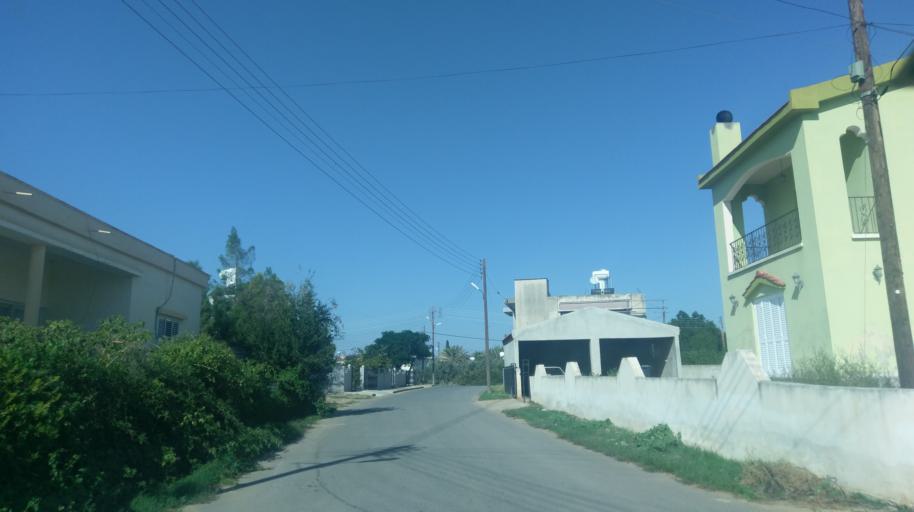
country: CY
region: Ammochostos
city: Lefkonoiko
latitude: 35.2383
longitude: 33.7808
